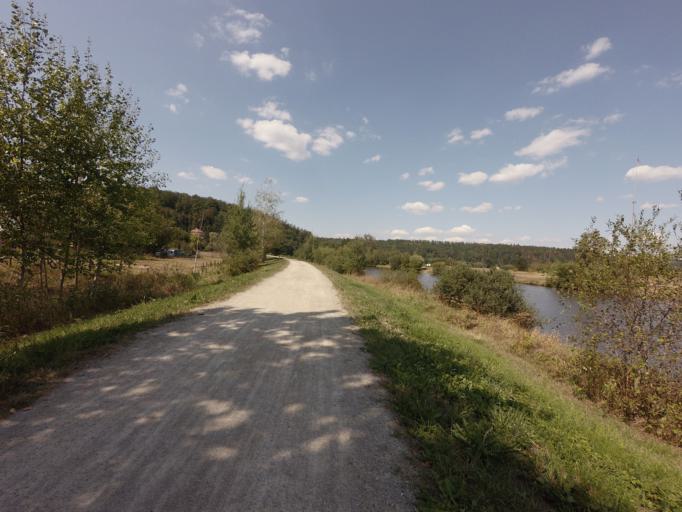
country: CZ
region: Jihocesky
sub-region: Okres Ceske Budejovice
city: Hluboka nad Vltavou
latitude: 49.0553
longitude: 14.4440
